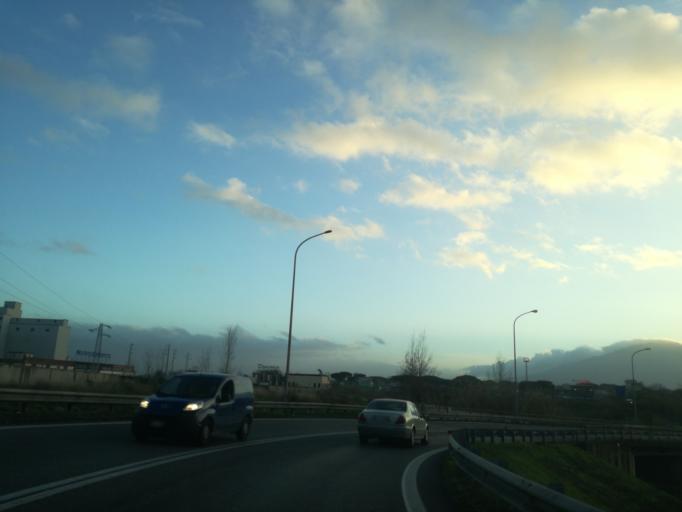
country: IT
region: Campania
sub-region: Provincia di Napoli
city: Cimitile
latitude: 40.9371
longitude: 14.5007
